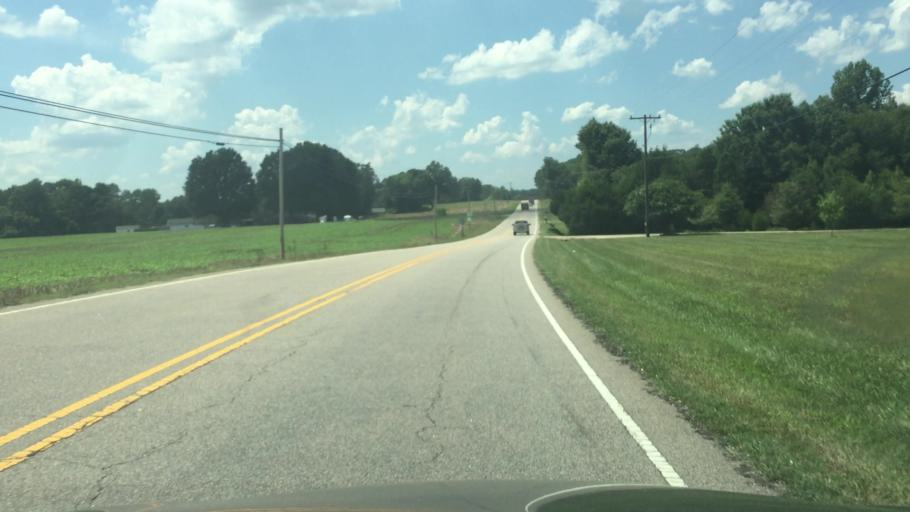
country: US
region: North Carolina
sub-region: Rowan County
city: Enochville
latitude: 35.5762
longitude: -80.7107
